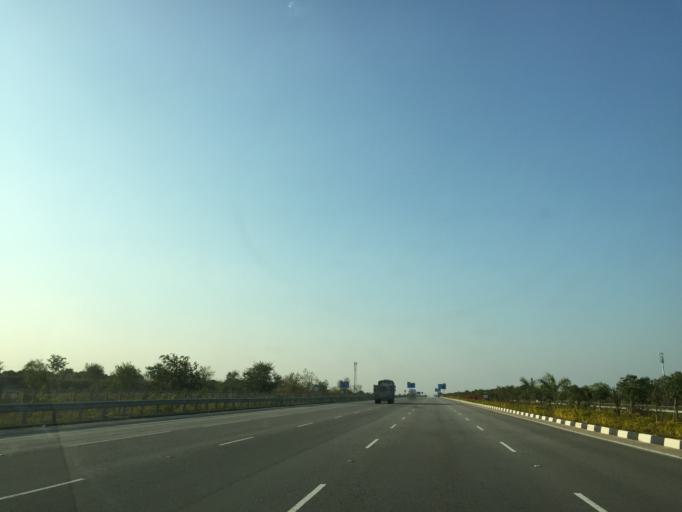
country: IN
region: Telangana
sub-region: Rangareddi
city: Ghatkesar
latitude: 17.5070
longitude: 78.6534
